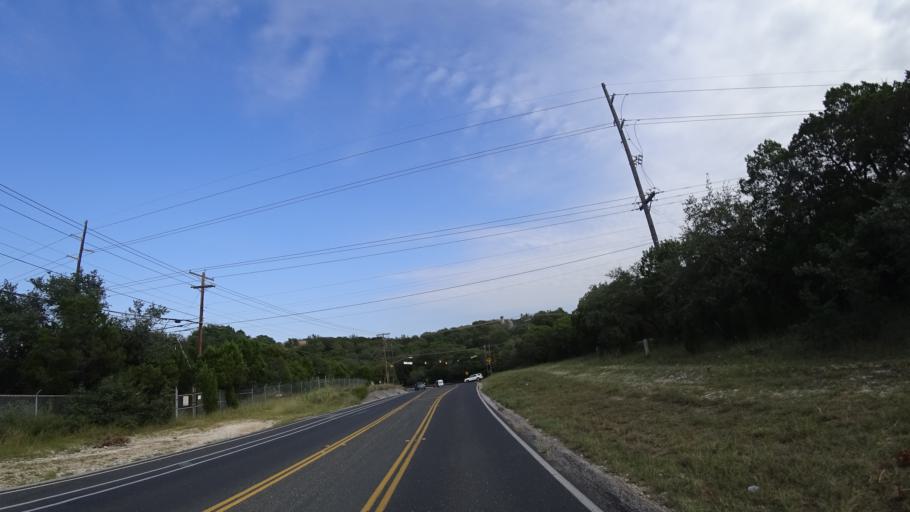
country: US
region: Texas
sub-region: Travis County
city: West Lake Hills
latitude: 30.2903
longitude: -97.7916
